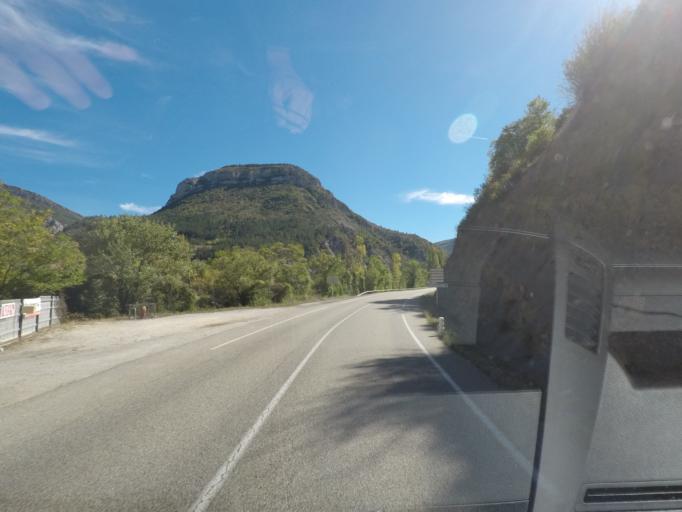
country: FR
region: Rhone-Alpes
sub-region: Departement de la Drome
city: Buis-les-Baronnies
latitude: 44.4116
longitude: 5.3476
